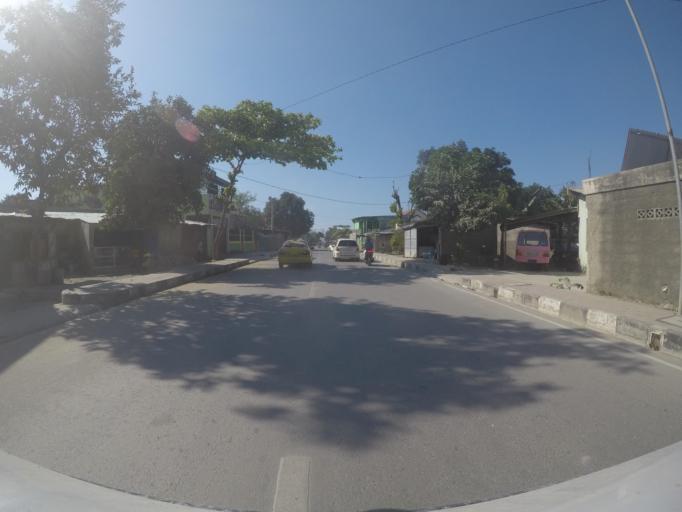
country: TL
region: Dili
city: Dili
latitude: -8.5619
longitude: 125.5558
